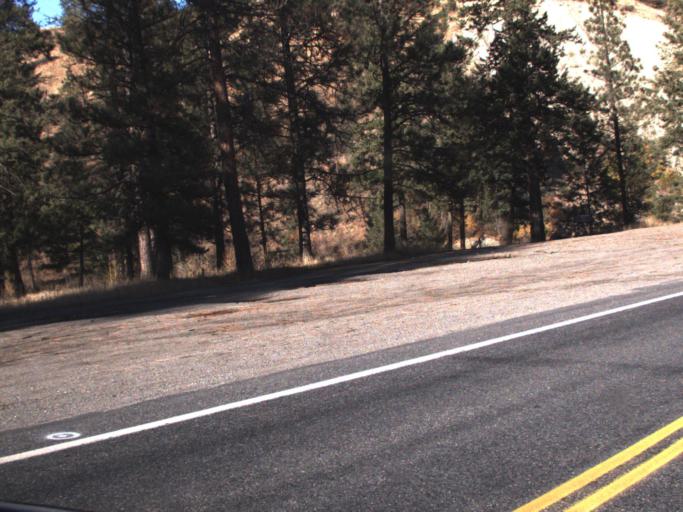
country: US
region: Washington
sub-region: Stevens County
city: Kettle Falls
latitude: 48.5727
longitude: -118.0886
